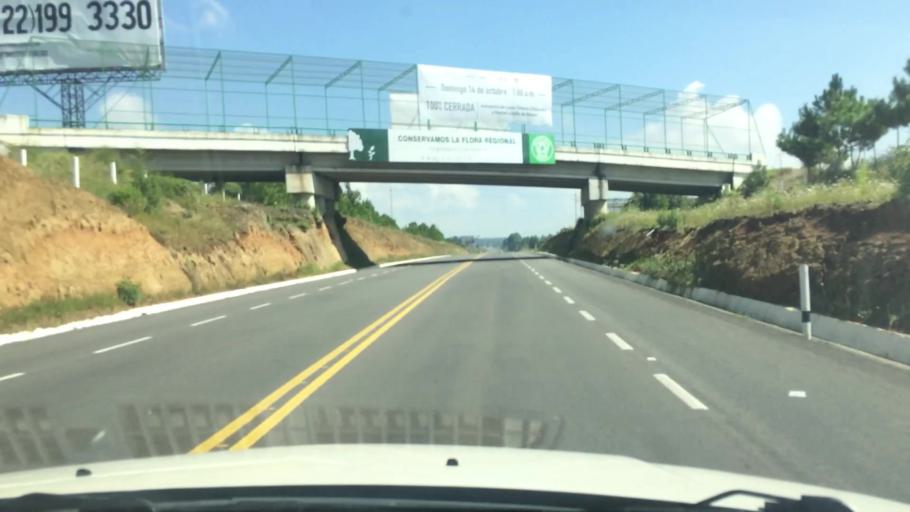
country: MX
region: Mexico
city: Amanalco de Becerra
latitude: 19.3050
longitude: -100.0093
